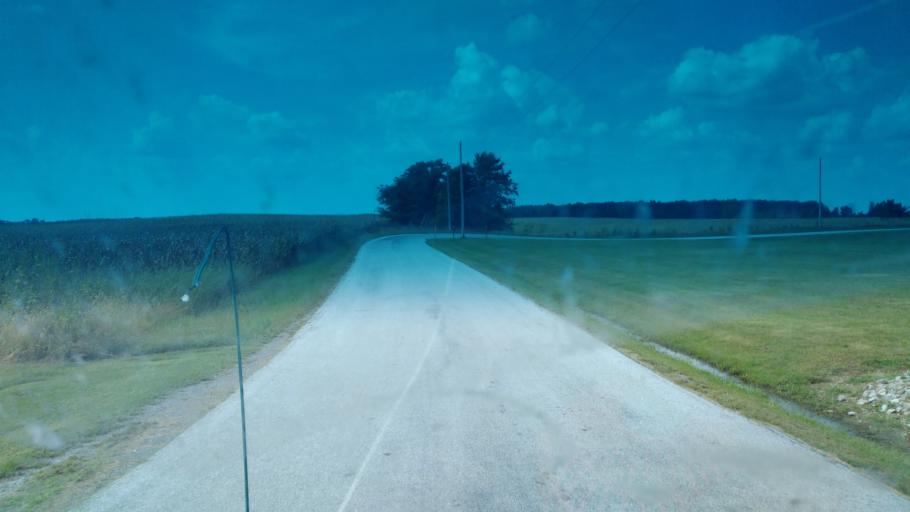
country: US
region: Ohio
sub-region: Hardin County
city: Kenton
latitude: 40.6364
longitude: -83.6540
